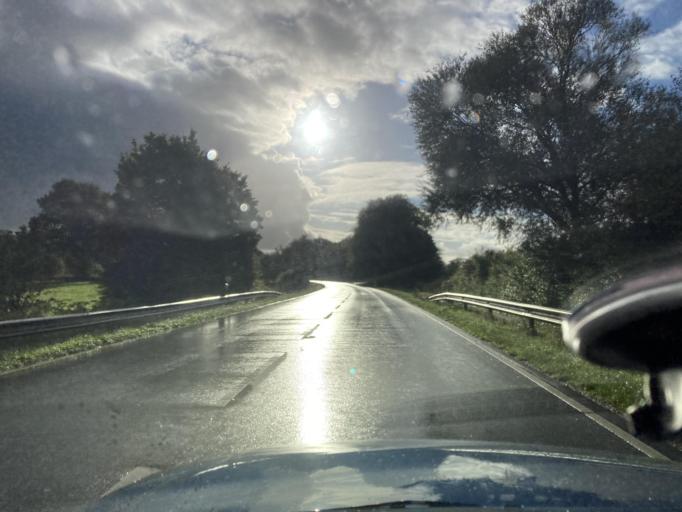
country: DE
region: Schleswig-Holstein
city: Tellingstedt
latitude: 54.2136
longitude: 9.2759
